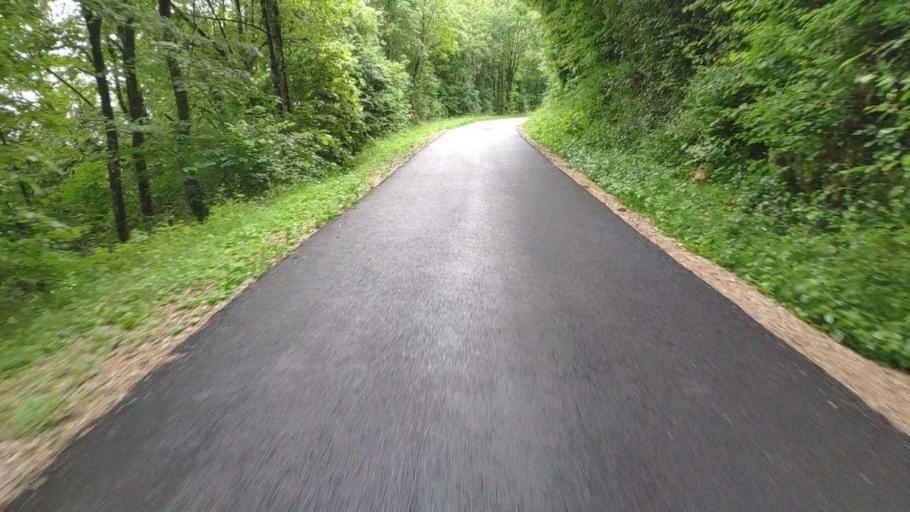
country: FR
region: Franche-Comte
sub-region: Departement du Jura
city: Poligny
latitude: 46.7925
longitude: 5.6240
